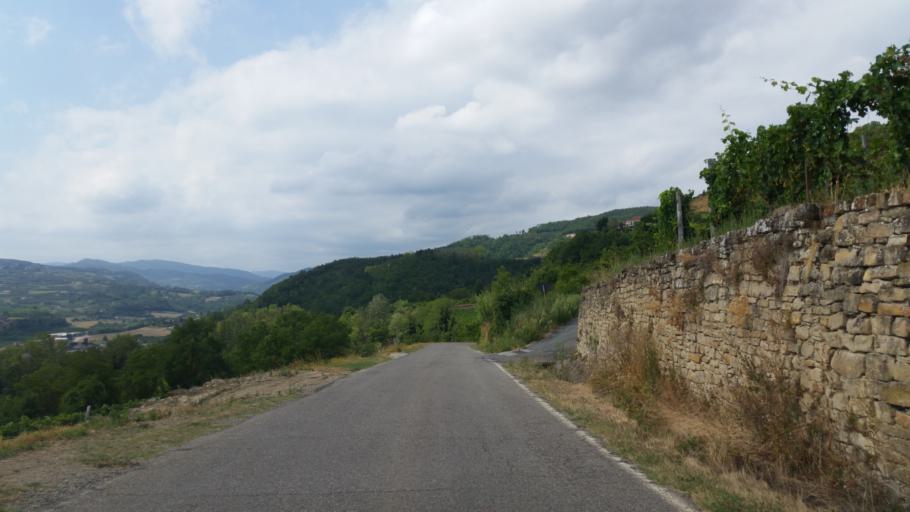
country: IT
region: Piedmont
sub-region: Provincia di Asti
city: Vesime
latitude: 44.6433
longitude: 8.2287
